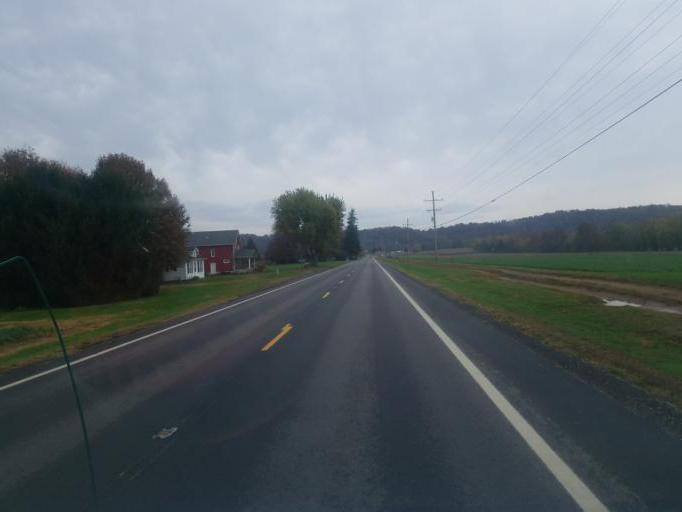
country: US
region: Ohio
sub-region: Washington County
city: Beverly
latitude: 39.5551
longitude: -81.5866
